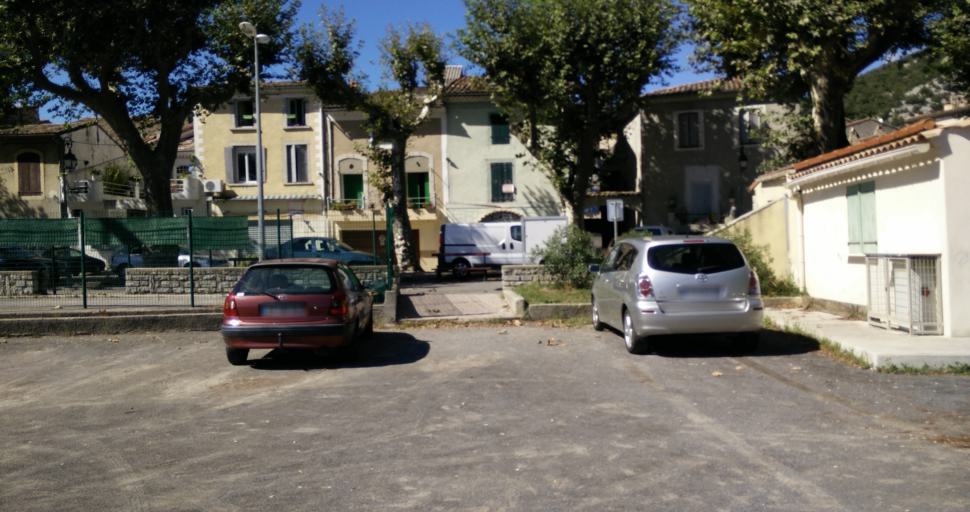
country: FR
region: Languedoc-Roussillon
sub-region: Departement du Gard
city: Saint-Hippolyte-du-Fort
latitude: 43.9642
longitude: 3.8586
